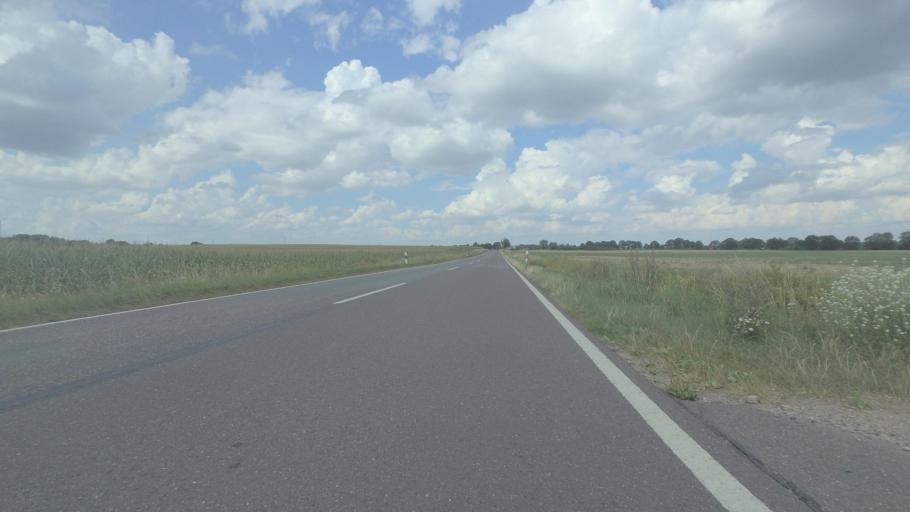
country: DE
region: Brandenburg
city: Wittstock
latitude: 53.2326
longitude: 12.4337
